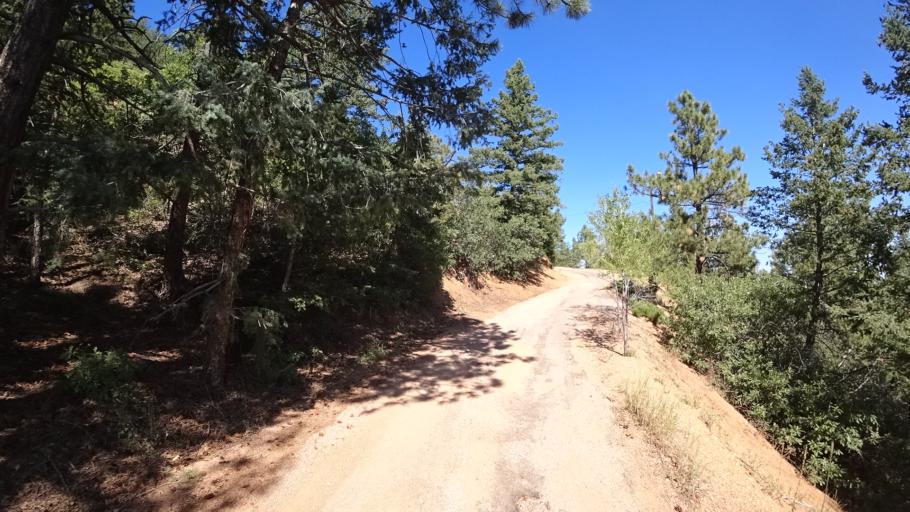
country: US
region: Colorado
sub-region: El Paso County
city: Manitou Springs
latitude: 38.8099
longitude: -104.8813
